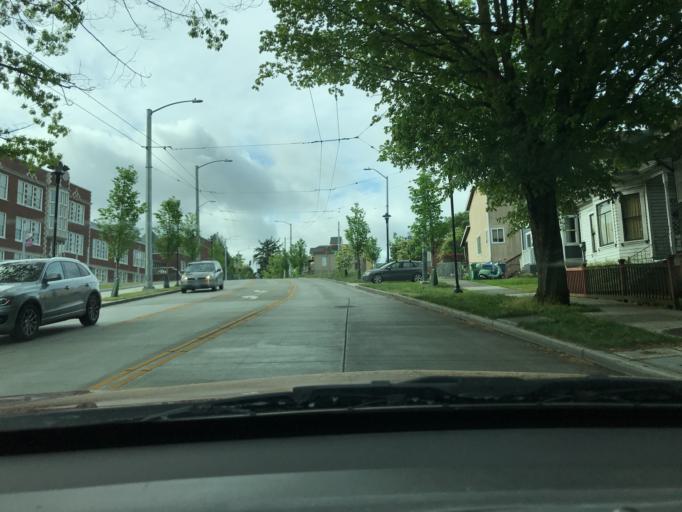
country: US
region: Washington
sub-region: King County
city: Seattle
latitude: 47.6061
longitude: -122.3029
